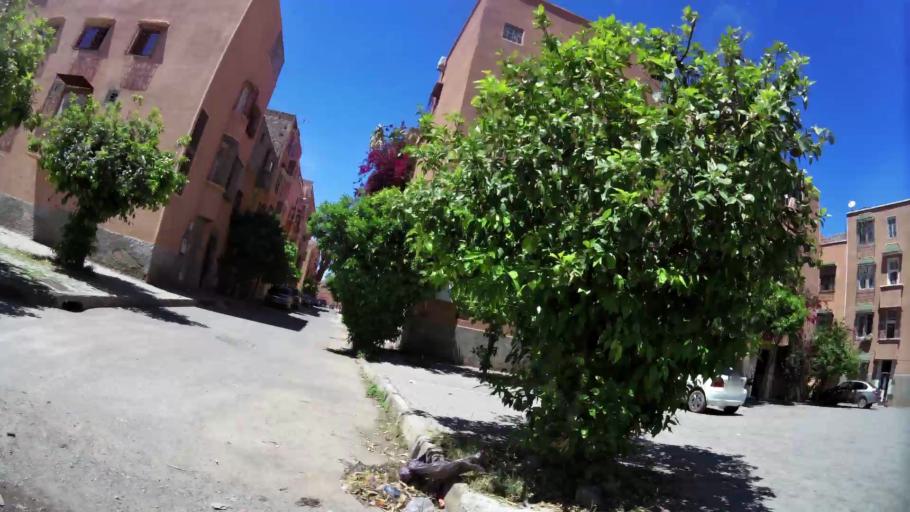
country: MA
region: Marrakech-Tensift-Al Haouz
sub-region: Marrakech
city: Marrakesh
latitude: 31.6287
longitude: -8.0518
